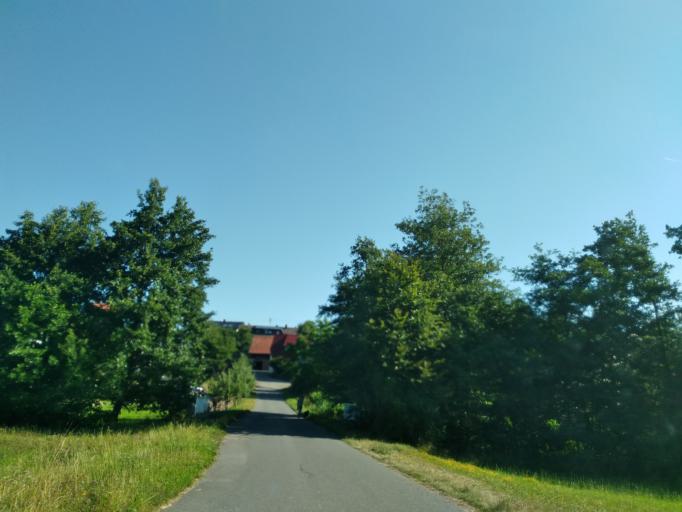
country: DE
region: Baden-Wuerttemberg
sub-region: Karlsruhe Region
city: Mudau
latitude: 49.5167
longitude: 9.1967
